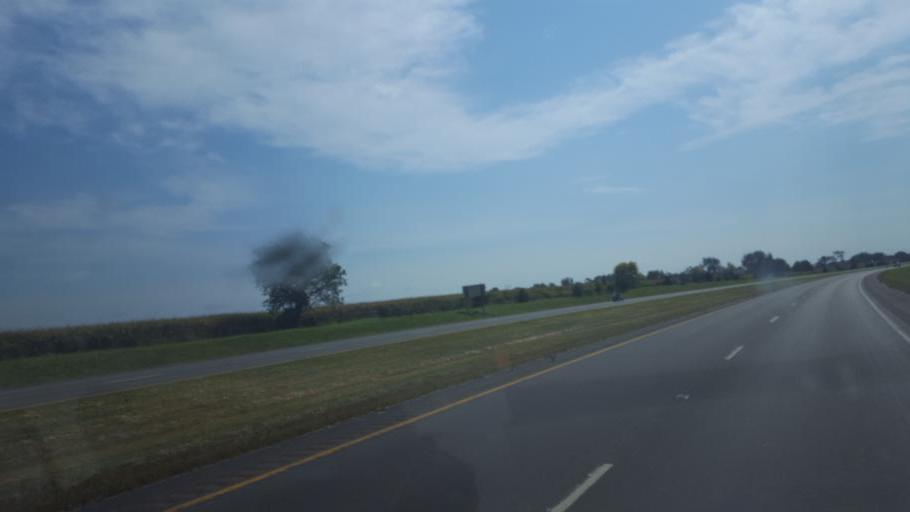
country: US
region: Ohio
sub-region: Knox County
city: Fredericktown
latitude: 40.4674
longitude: -82.5496
